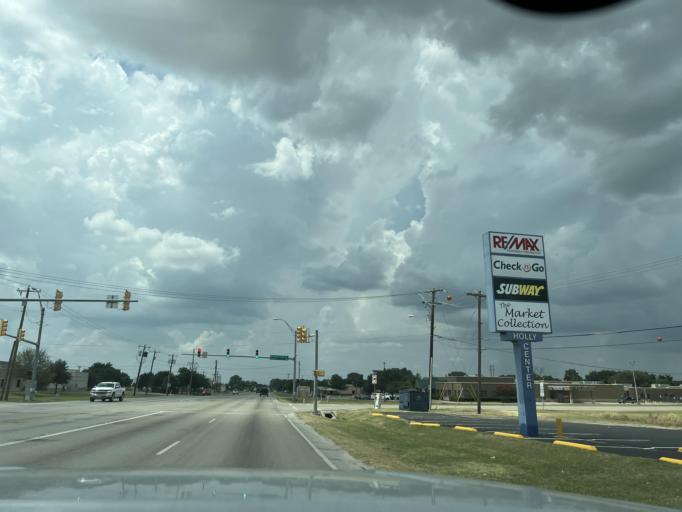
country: US
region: Texas
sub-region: Wise County
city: Decatur
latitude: 33.2191
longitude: -97.5959
